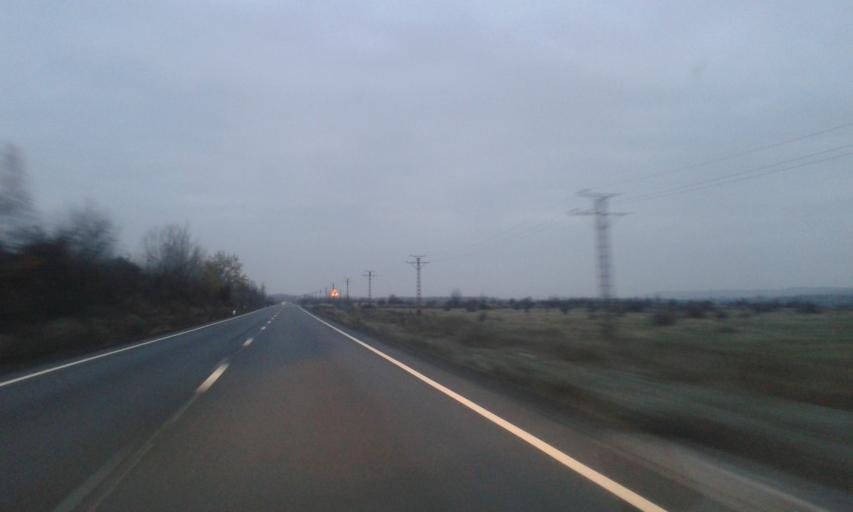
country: RO
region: Gorj
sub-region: Comuna Bumbesti-Jiu
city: Bumbesti-Jiu
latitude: 45.1507
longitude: 23.3724
